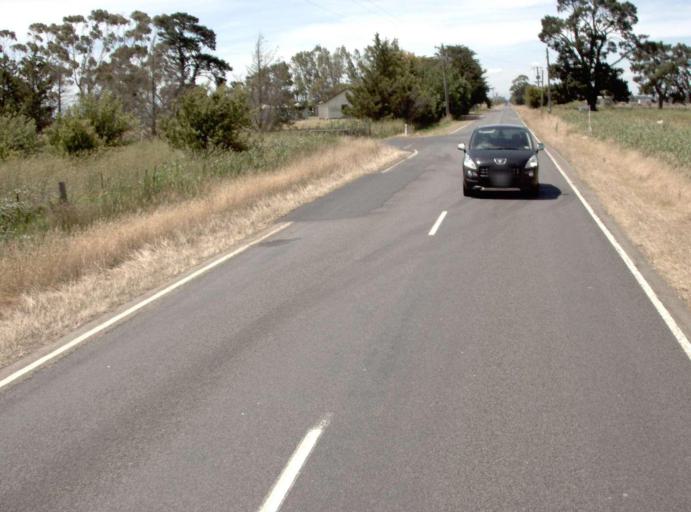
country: AU
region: Victoria
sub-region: Wellington
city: Heyfield
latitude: -38.0893
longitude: 146.8667
